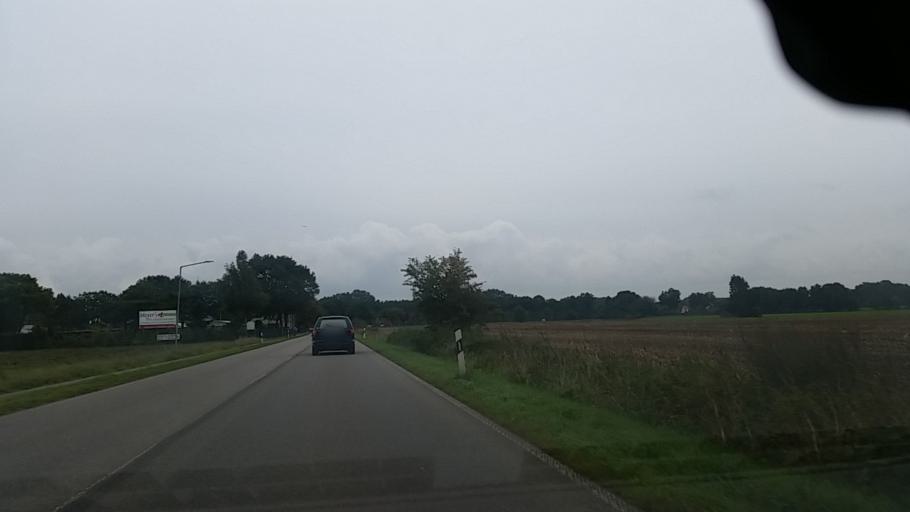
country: DE
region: Schleswig-Holstein
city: Kayhude
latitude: 53.7625
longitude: 10.1287
